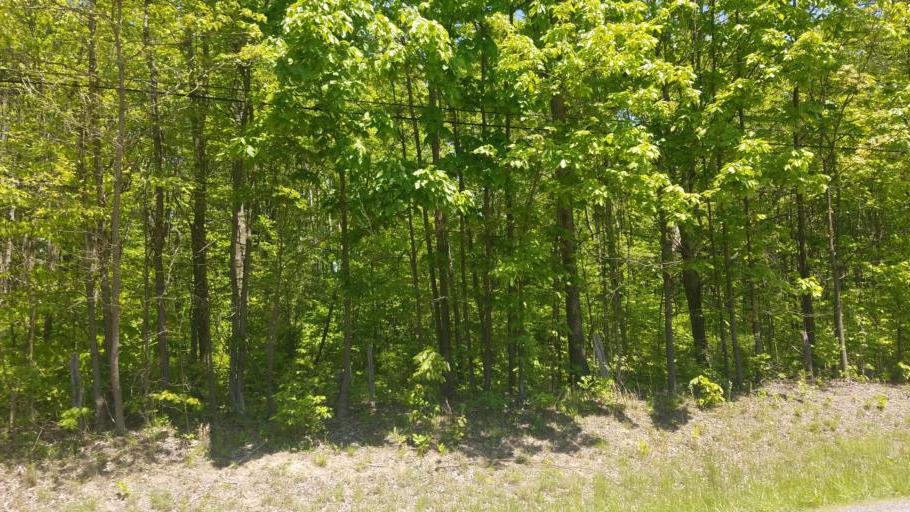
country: US
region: Ohio
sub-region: Muskingum County
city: Frazeysburg
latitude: 40.2265
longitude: -82.2665
